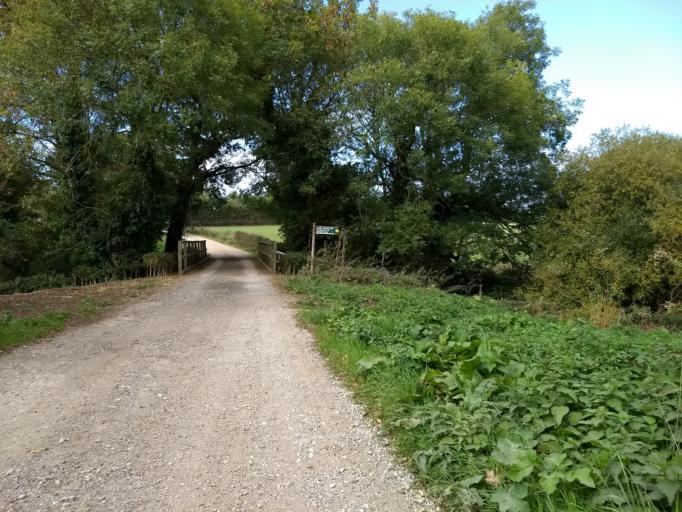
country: GB
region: England
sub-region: Isle of Wight
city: Seaview
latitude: 50.7100
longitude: -1.1275
